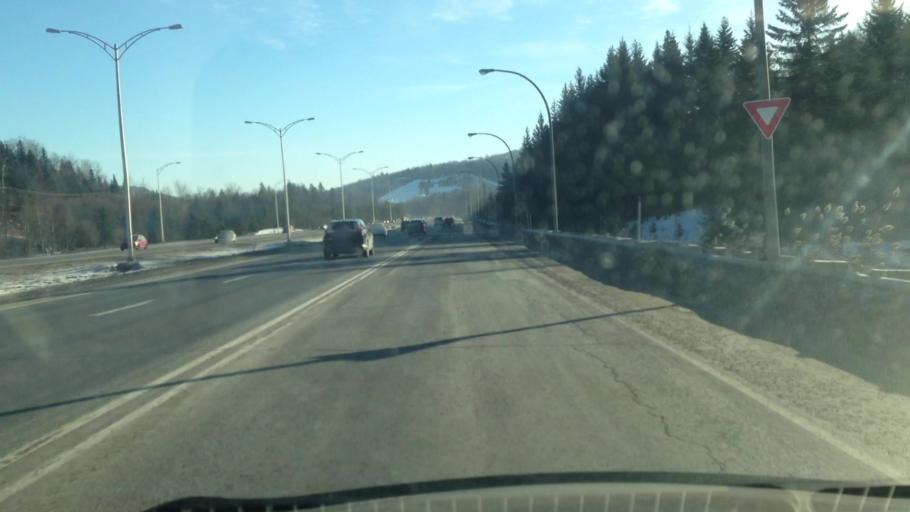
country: CA
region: Quebec
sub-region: Laurentides
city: Saint-Sauveur
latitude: 45.8893
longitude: -74.1421
